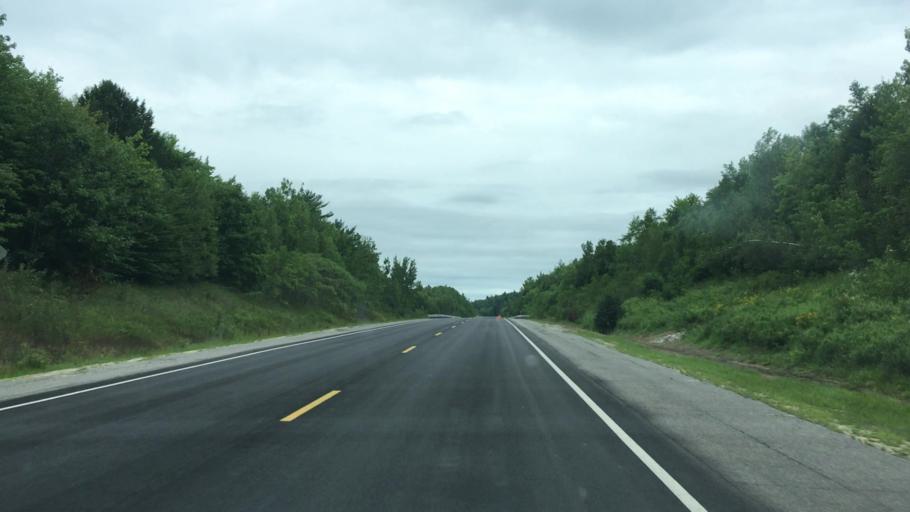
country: US
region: Maine
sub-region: Washington County
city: Cherryfield
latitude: 44.8877
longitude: -67.8567
